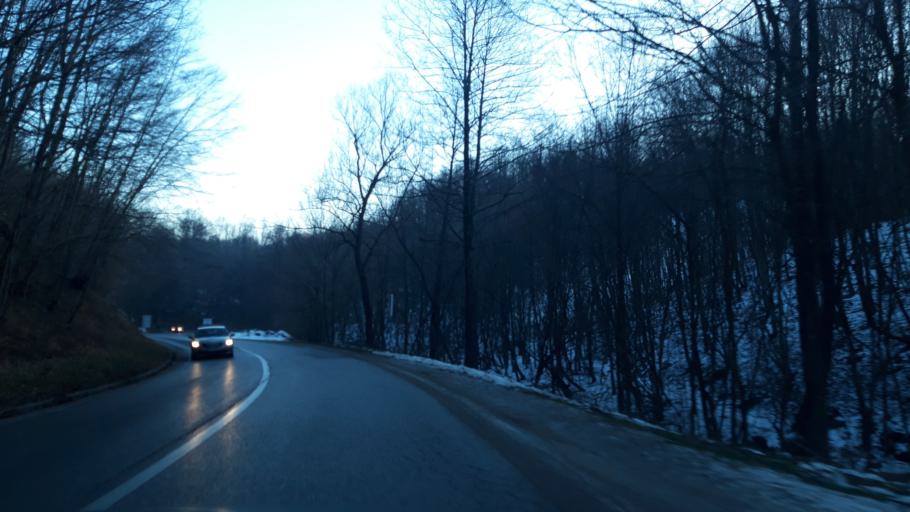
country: BA
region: Republika Srpska
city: Vlasenica
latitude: 44.1823
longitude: 19.0078
